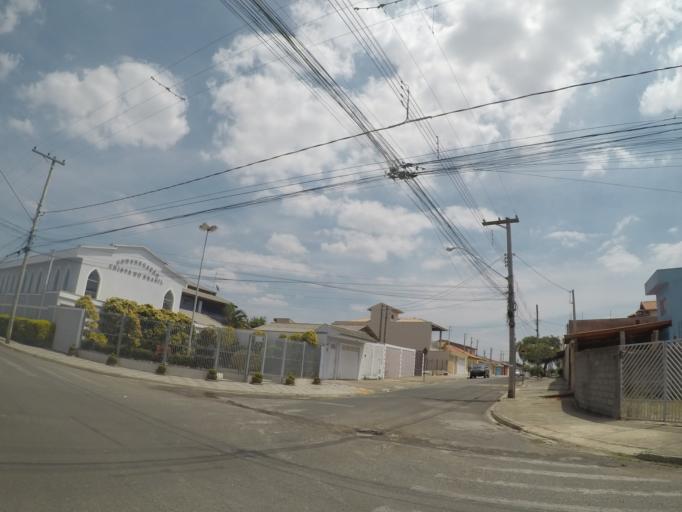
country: BR
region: Sao Paulo
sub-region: Cabreuva
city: Cabreuva
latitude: -23.2601
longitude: -47.0478
